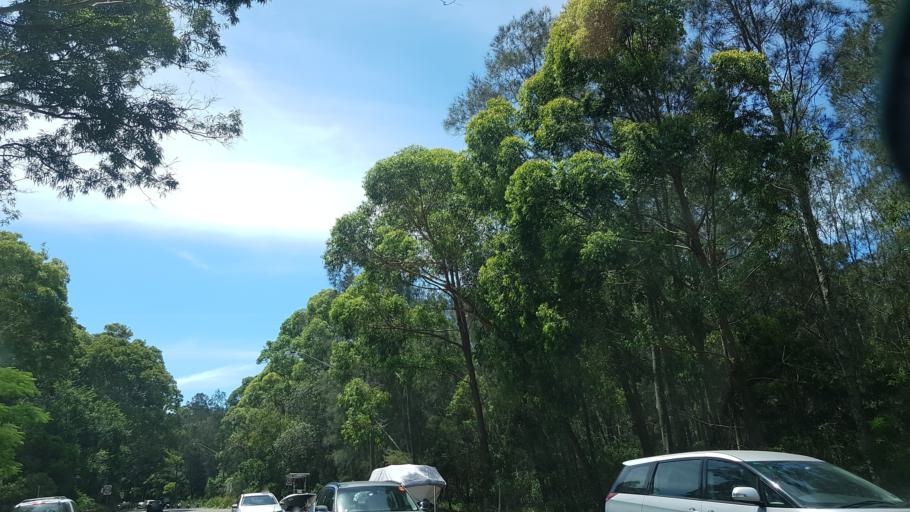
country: AU
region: New South Wales
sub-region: Pittwater
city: Bay View
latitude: -33.6660
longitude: 151.3014
